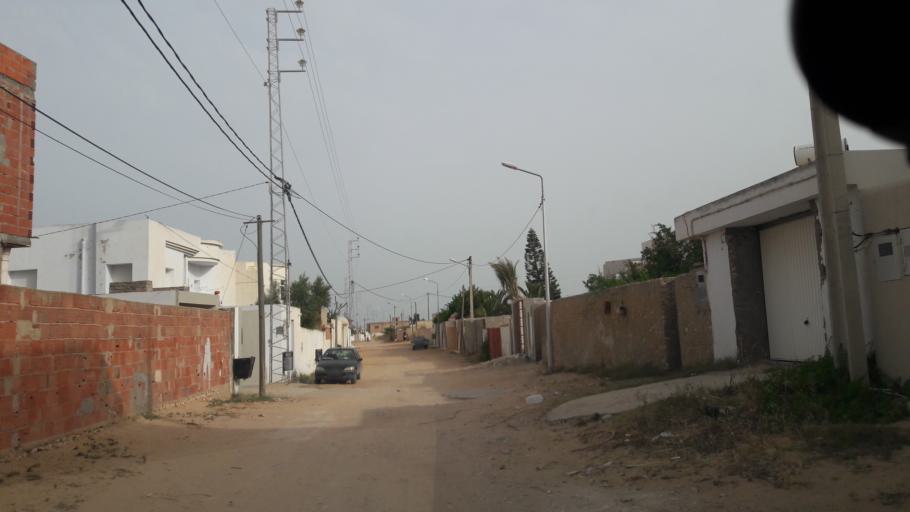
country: TN
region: Safaqis
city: Al Qarmadah
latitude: 34.7805
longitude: 10.7697
